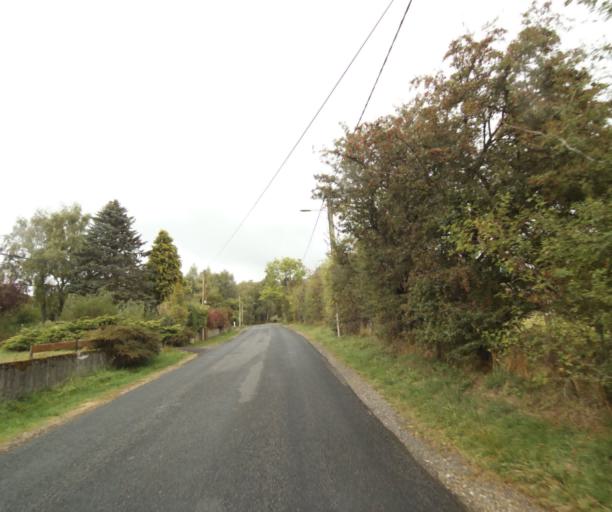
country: FR
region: Auvergne
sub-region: Departement du Puy-de-Dome
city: Saint-Genes-Champanelle
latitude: 45.7379
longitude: 2.9703
